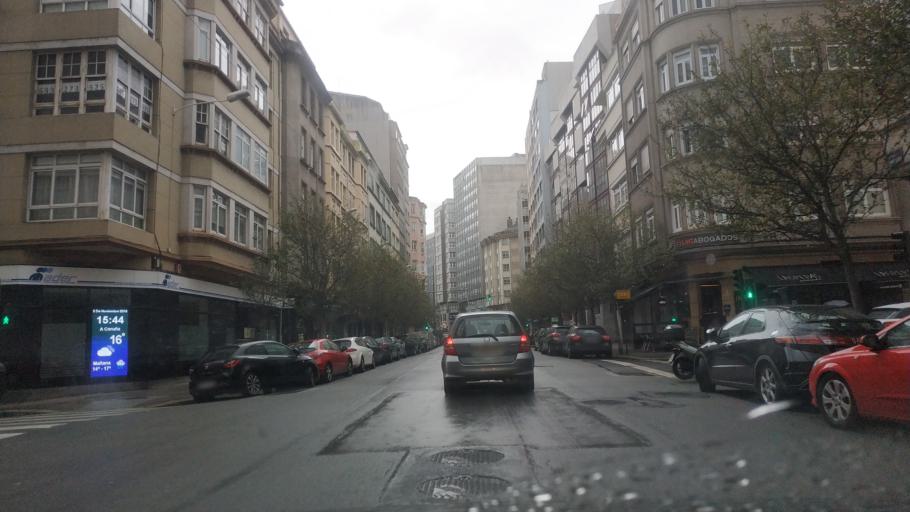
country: ES
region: Galicia
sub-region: Provincia da Coruna
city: A Coruna
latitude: 43.3632
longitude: -8.4081
